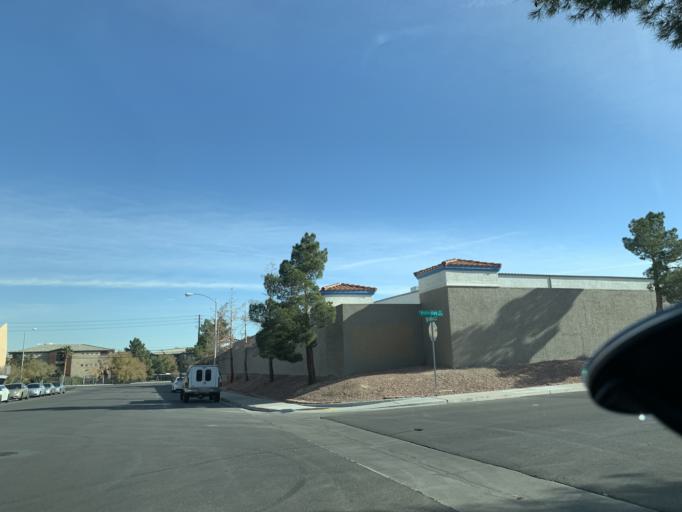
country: US
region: Nevada
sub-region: Clark County
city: Spring Valley
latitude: 36.1104
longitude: -115.2262
